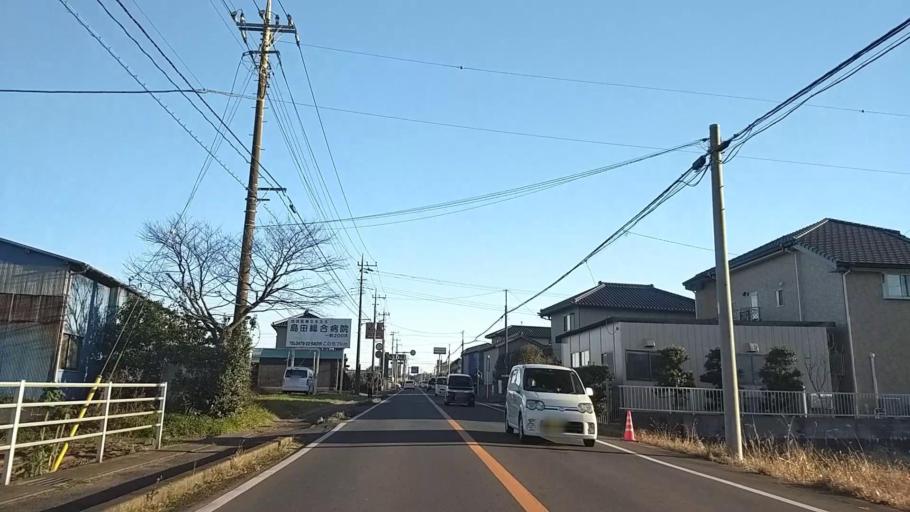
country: JP
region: Chiba
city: Hasaki
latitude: 35.7569
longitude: 140.7714
